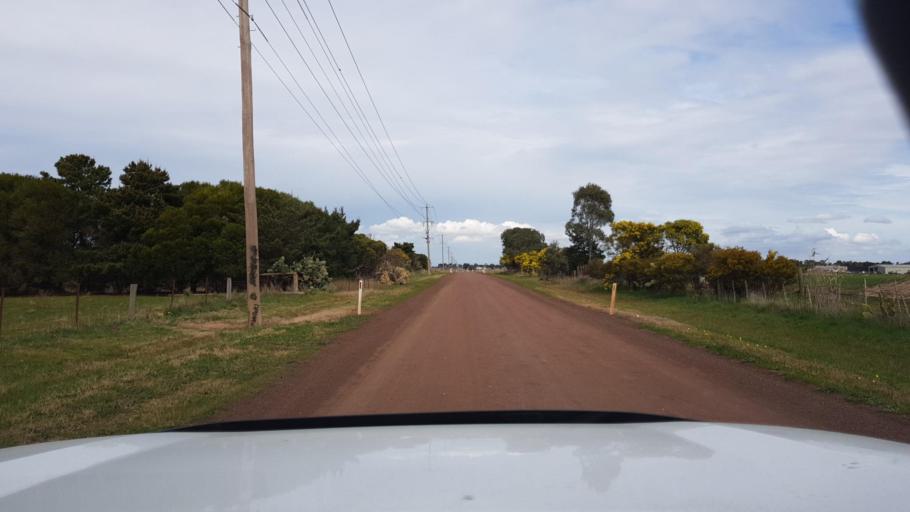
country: AU
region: Victoria
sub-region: Melton
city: Kurunjang
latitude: -37.6616
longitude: 144.6184
